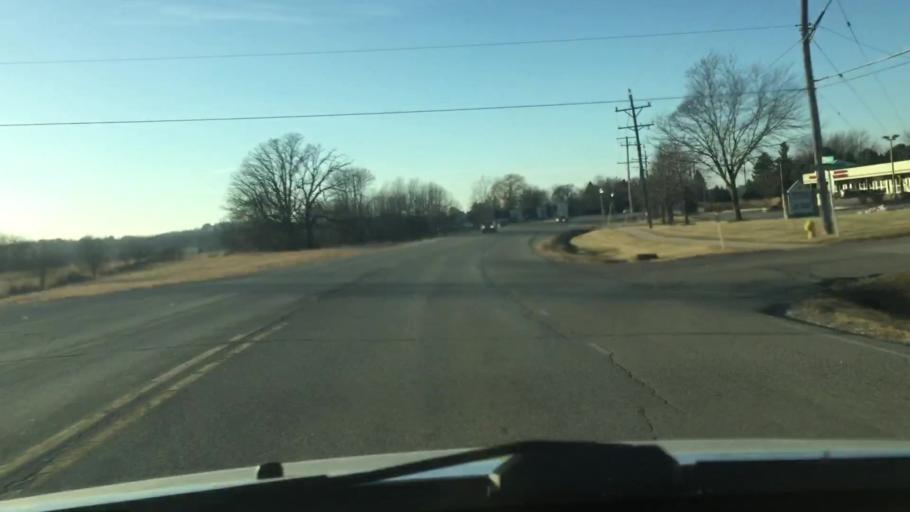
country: US
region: Wisconsin
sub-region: Waukesha County
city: Sussex
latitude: 43.1340
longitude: -88.2361
